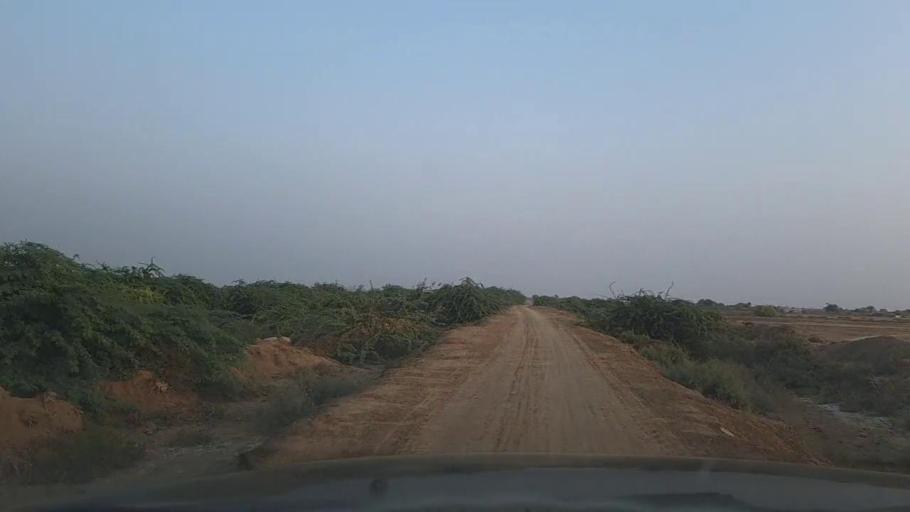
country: PK
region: Sindh
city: Jati
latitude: 24.5425
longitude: 68.3963
